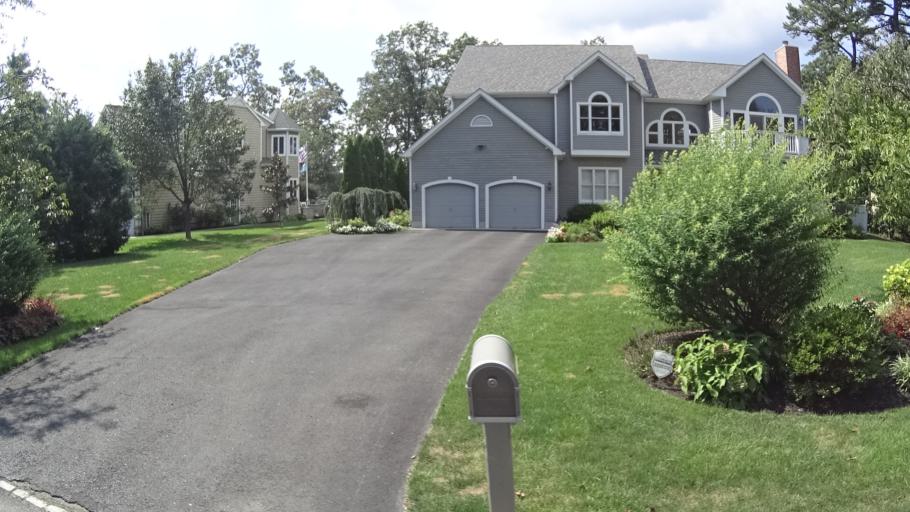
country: US
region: New Jersey
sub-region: Monmouth County
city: Brielle
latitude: 40.1094
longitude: -74.0889
